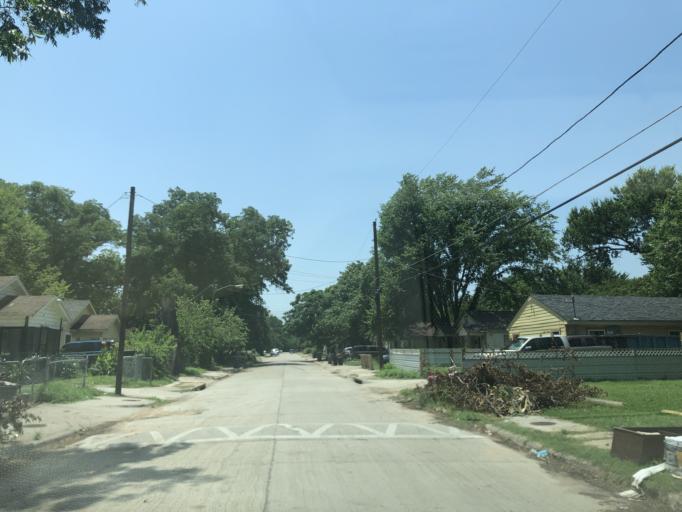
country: US
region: Texas
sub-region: Dallas County
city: Dallas
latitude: 32.7750
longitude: -96.8374
